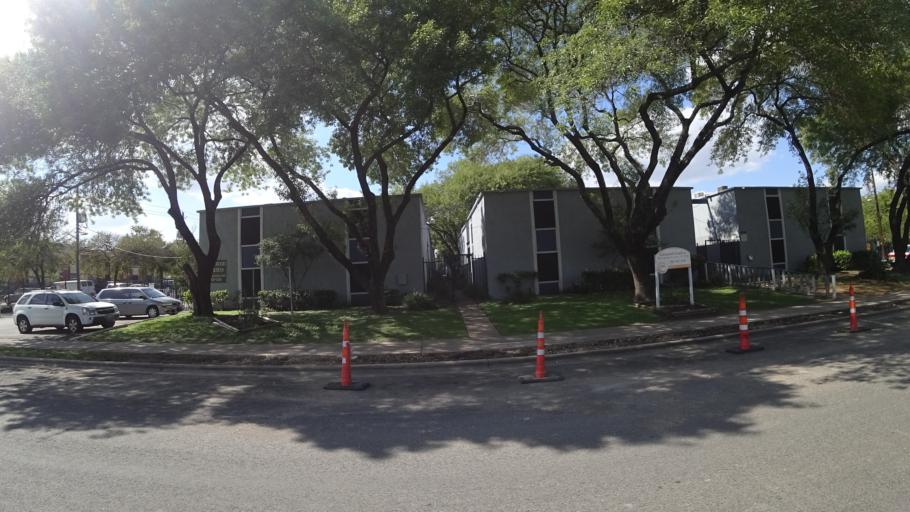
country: US
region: Texas
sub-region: Travis County
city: Wells Branch
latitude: 30.3677
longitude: -97.7149
